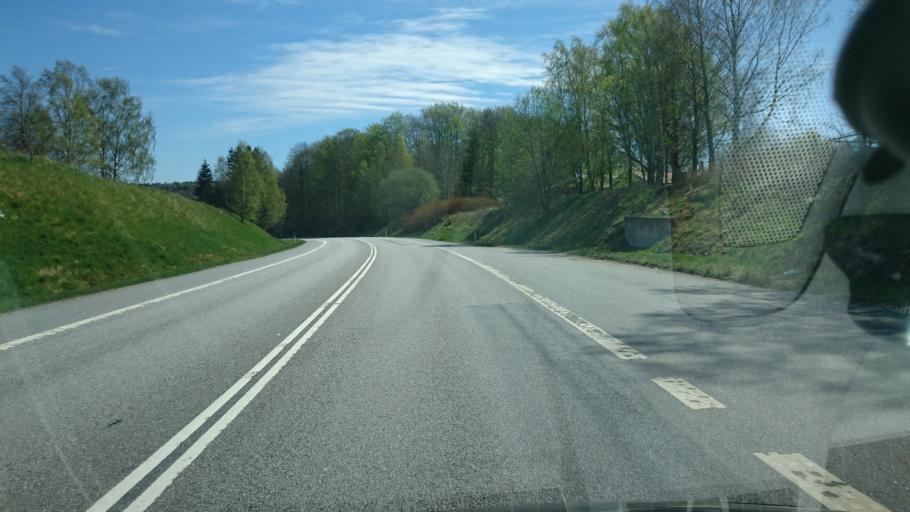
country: SE
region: Vaestra Goetaland
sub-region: Munkedals Kommun
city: Munkedal
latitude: 58.4701
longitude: 11.6648
